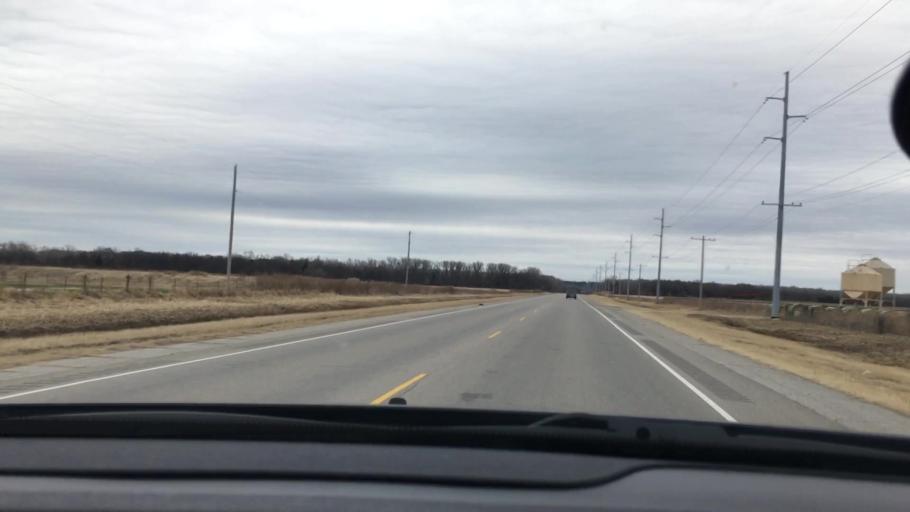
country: US
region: Oklahoma
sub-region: Marshall County
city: Oakland
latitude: 34.2081
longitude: -96.8022
